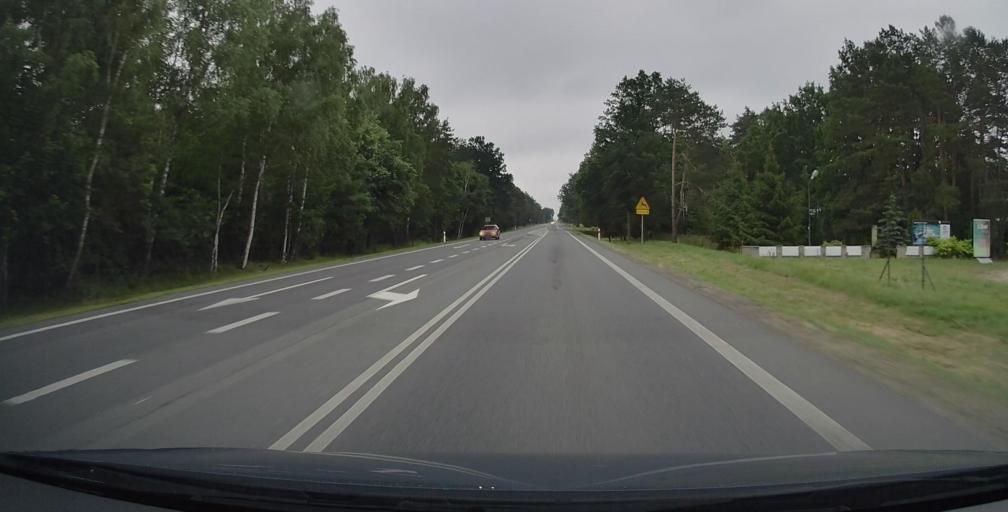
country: PL
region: Lublin Voivodeship
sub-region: Biala Podlaska
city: Biala Podlaska
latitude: 52.0381
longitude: 23.2119
